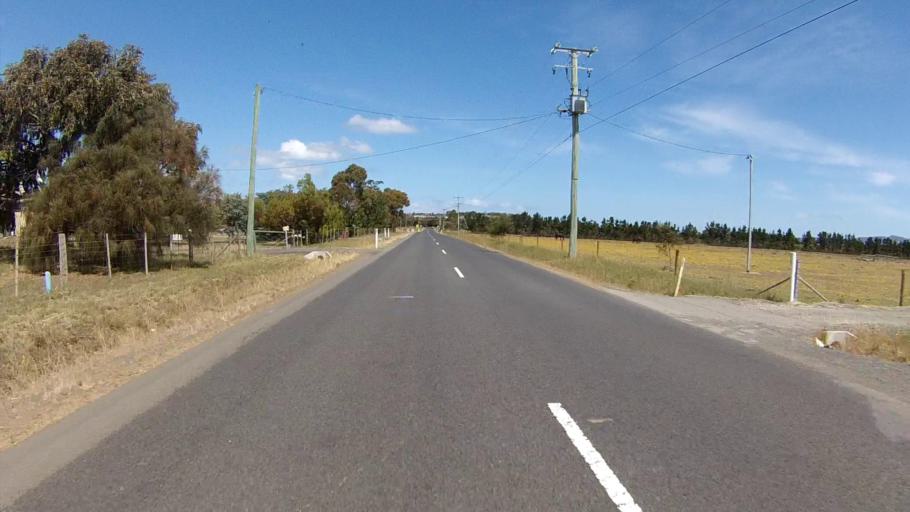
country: AU
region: Tasmania
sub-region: Sorell
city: Sorell
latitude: -42.7753
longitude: 147.5198
